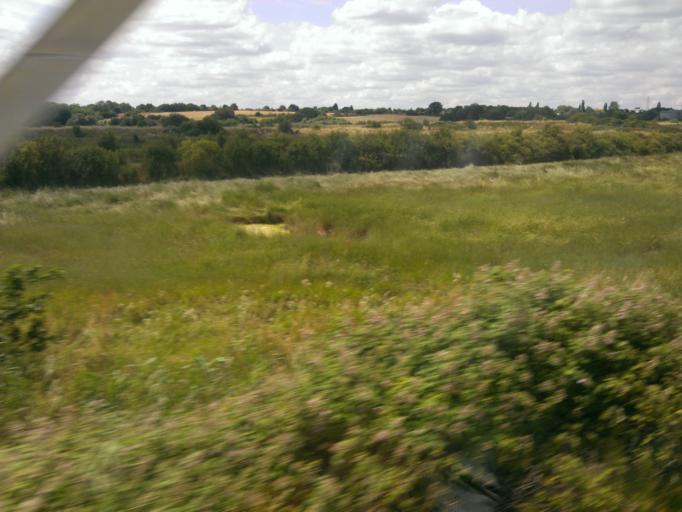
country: GB
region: England
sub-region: Essex
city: Rowhedge
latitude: 51.8690
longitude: 0.9440
